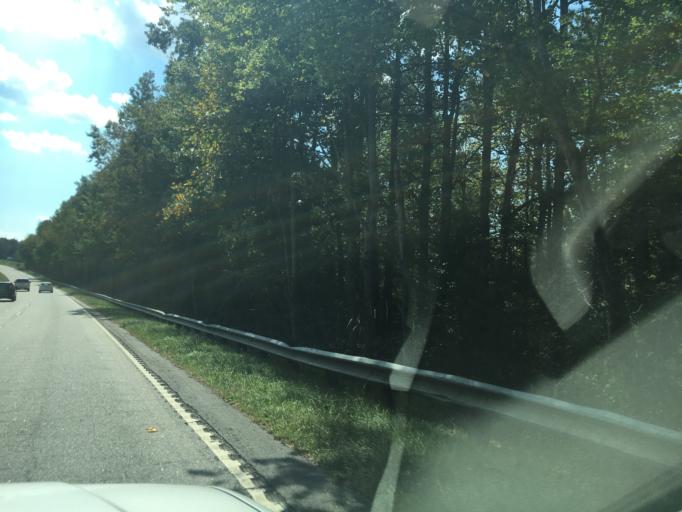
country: US
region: South Carolina
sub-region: Pickens County
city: Liberty
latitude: 34.7470
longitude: -82.7135
